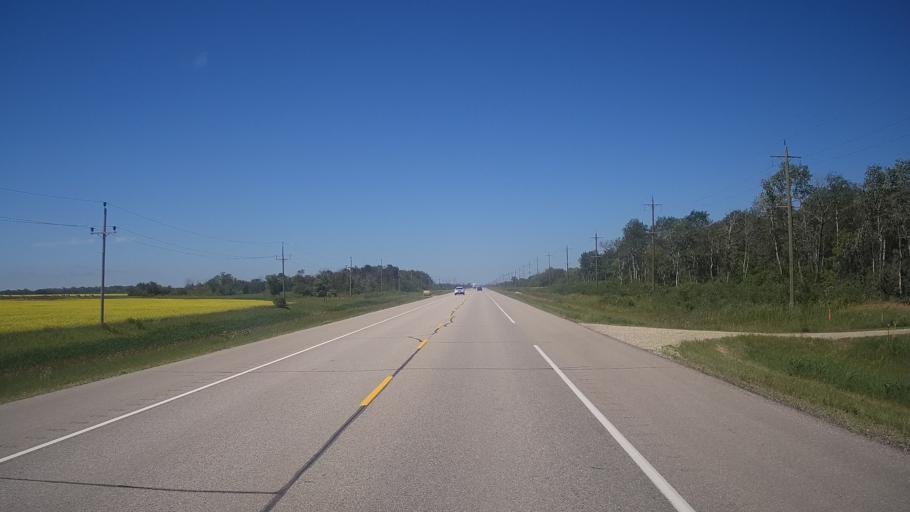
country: CA
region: Manitoba
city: Neepawa
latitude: 50.2258
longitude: -99.0961
